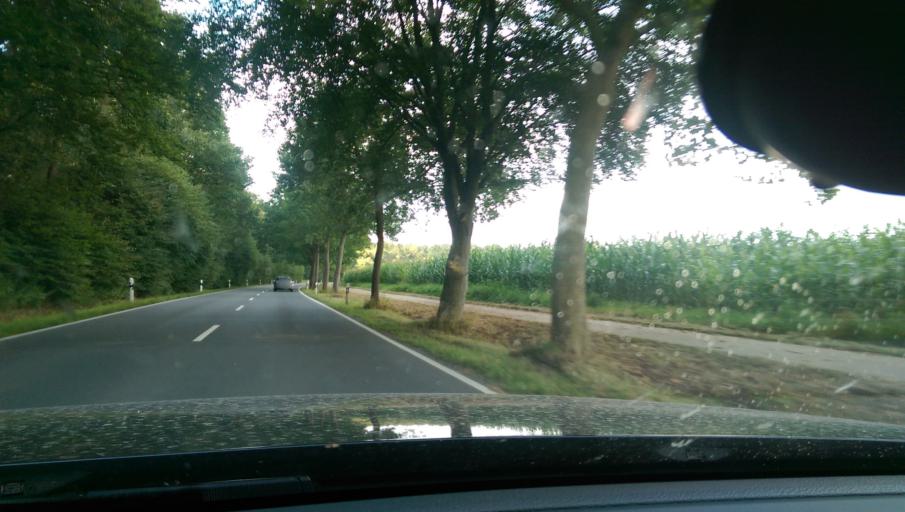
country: DE
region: Lower Saxony
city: Neustadt am Rubenberge
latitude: 52.5510
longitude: 9.4780
